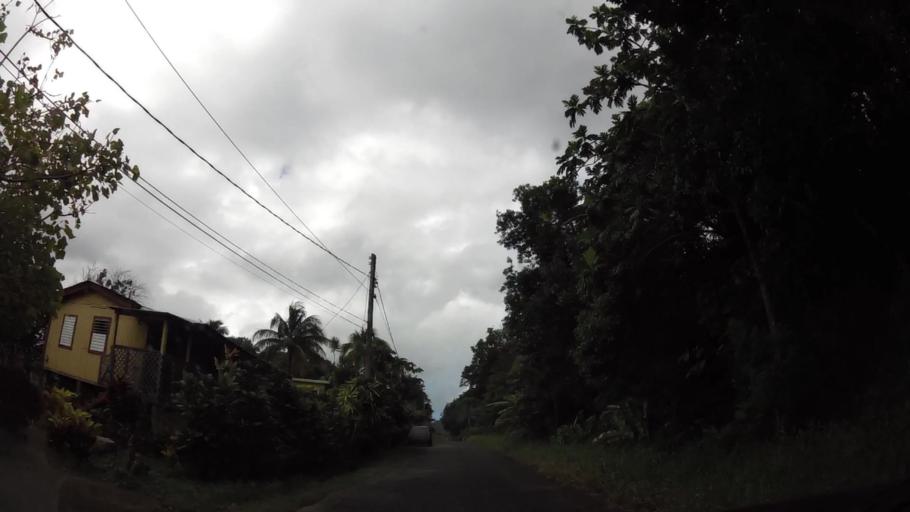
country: DM
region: Saint David
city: Castle Bruce
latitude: 15.4471
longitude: -61.2570
